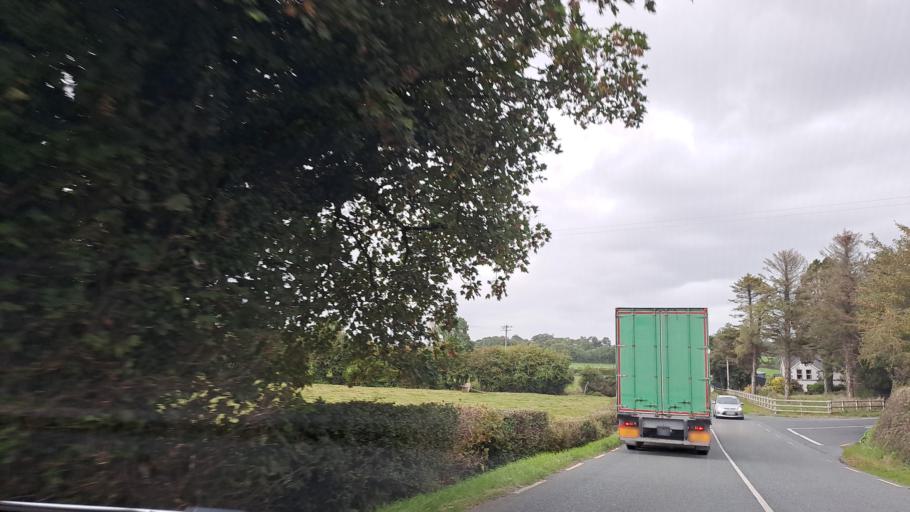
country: IE
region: Ulster
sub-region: County Monaghan
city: Monaghan
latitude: 54.1372
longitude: -6.9124
